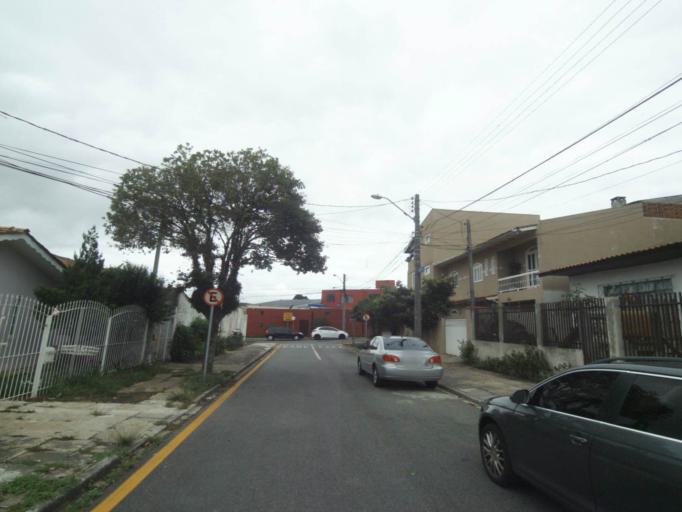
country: BR
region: Parana
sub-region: Curitiba
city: Curitiba
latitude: -25.4939
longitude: -49.2817
